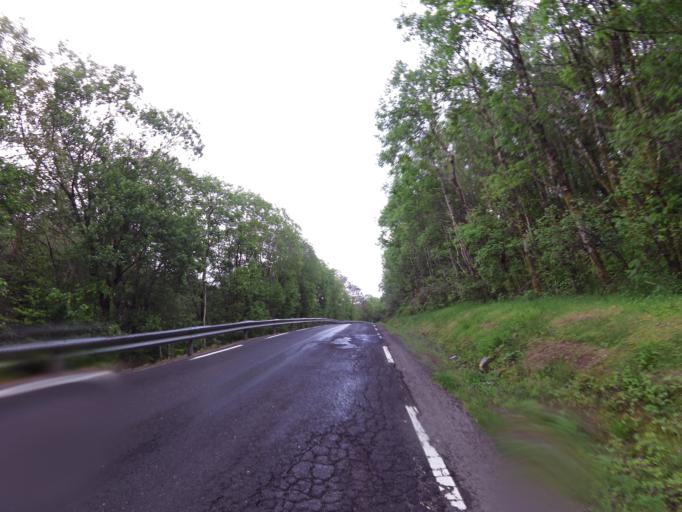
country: NO
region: Vest-Agder
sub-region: Lyngdal
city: Lyngdal
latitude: 58.1151
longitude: 7.0759
